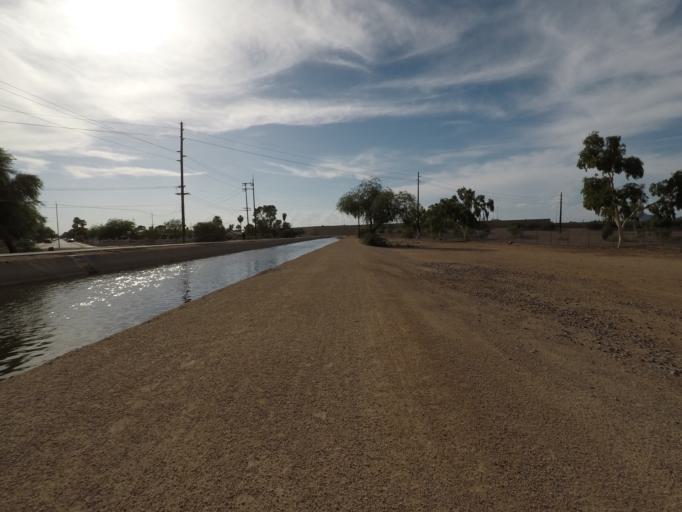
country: US
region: Arizona
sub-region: Maricopa County
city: Phoenix
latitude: 33.4567
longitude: -112.0033
